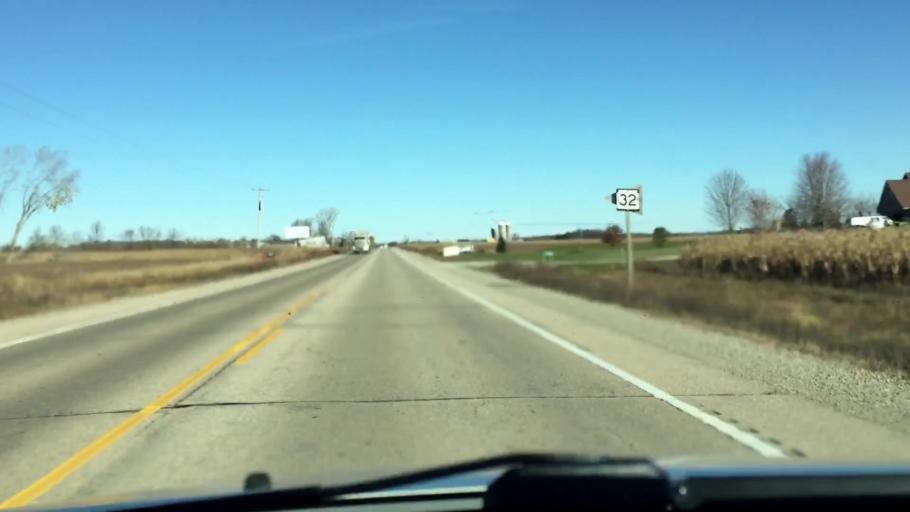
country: US
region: Wisconsin
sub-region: Brown County
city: Pulaski
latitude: 44.6166
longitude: -88.2205
